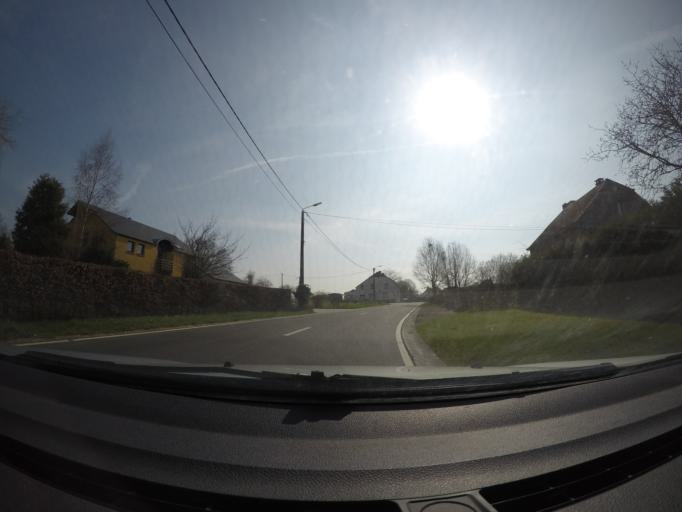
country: BE
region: Wallonia
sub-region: Province du Luxembourg
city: Tintigny
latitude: 49.7045
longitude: 5.4272
